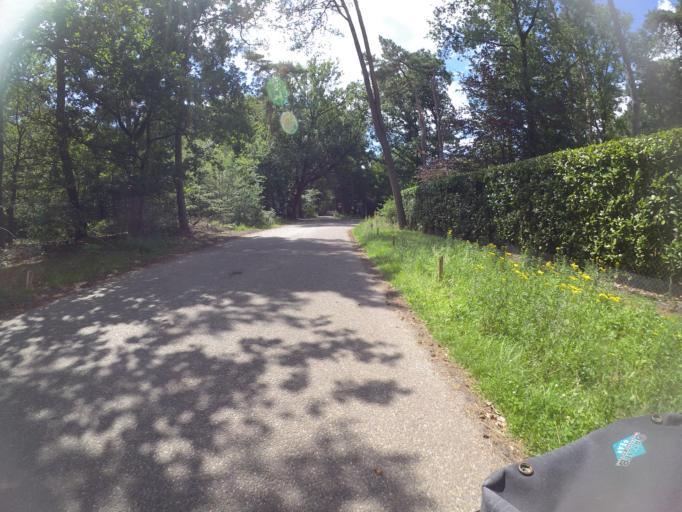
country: NL
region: North Brabant
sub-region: Gemeente Oisterwijk
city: Oisterwijk
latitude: 51.5658
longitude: 5.2033
